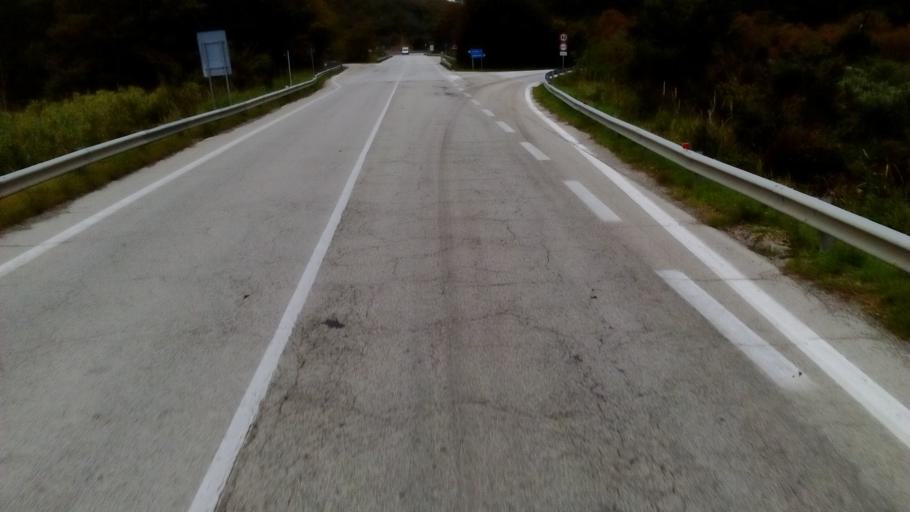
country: IT
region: Molise
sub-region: Provincia di Campobasso
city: Montemitro
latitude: 41.9033
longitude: 14.6449
